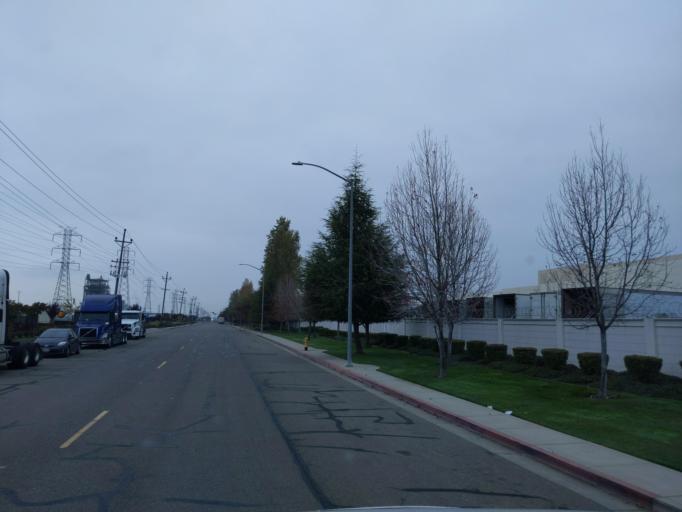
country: US
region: California
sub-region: San Joaquin County
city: Kennedy
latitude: 37.9153
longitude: -121.2553
